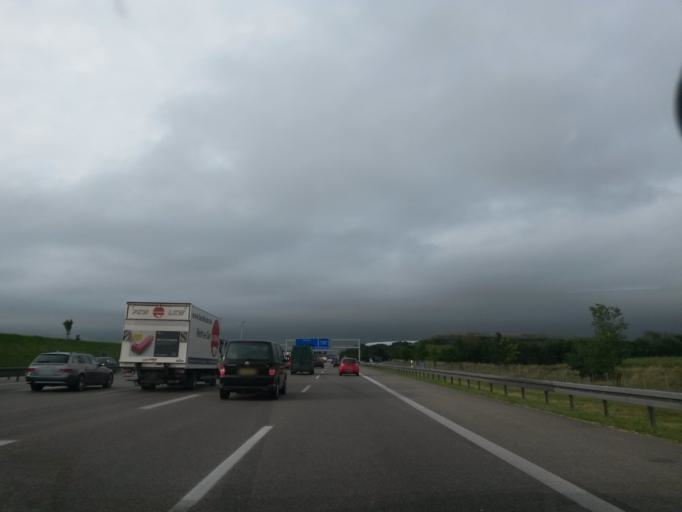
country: DE
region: Bavaria
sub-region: Upper Bavaria
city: Garching bei Munchen
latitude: 48.2330
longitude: 11.6350
